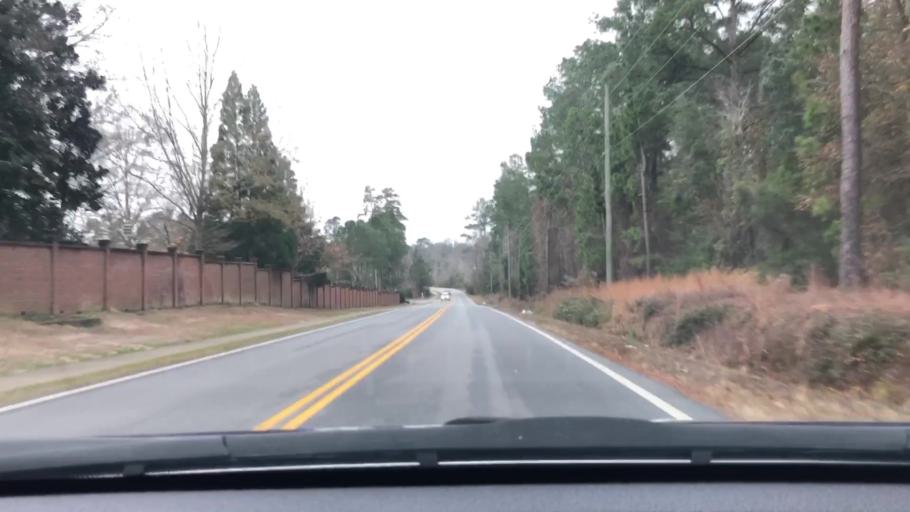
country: US
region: South Carolina
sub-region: Sumter County
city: Cherryvale
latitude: 33.9508
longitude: -80.4020
